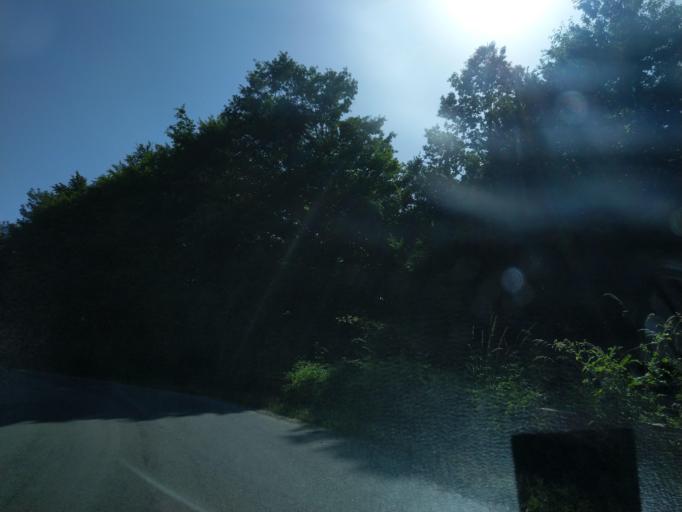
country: RS
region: Central Serbia
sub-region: Zlatiborski Okrug
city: Uzice
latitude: 43.8729
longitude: 19.7276
